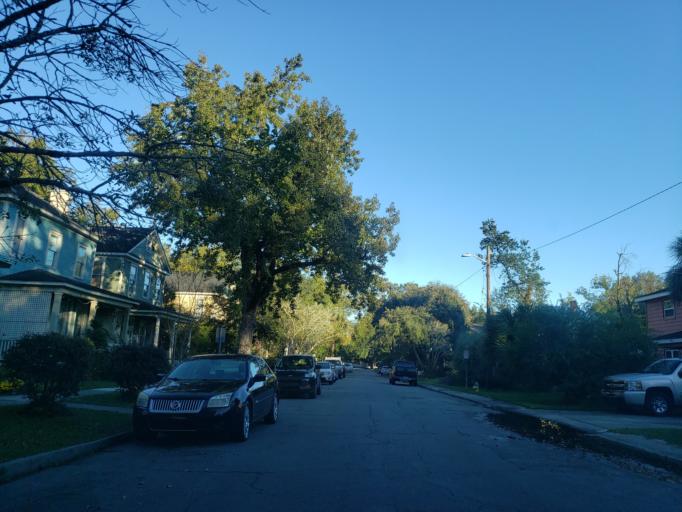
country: US
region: Georgia
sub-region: Chatham County
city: Savannah
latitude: 32.0612
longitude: -81.0866
